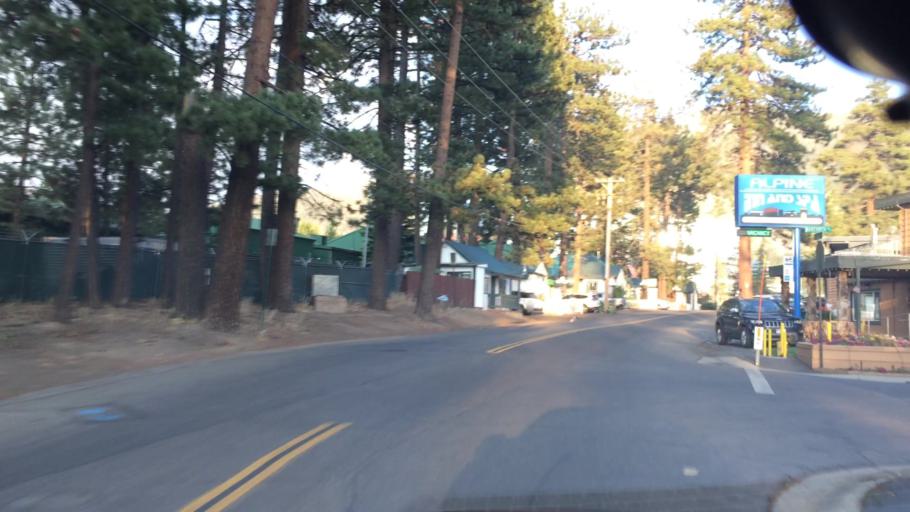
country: US
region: Nevada
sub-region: Douglas County
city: Kingsbury
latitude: 38.9611
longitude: -119.9453
